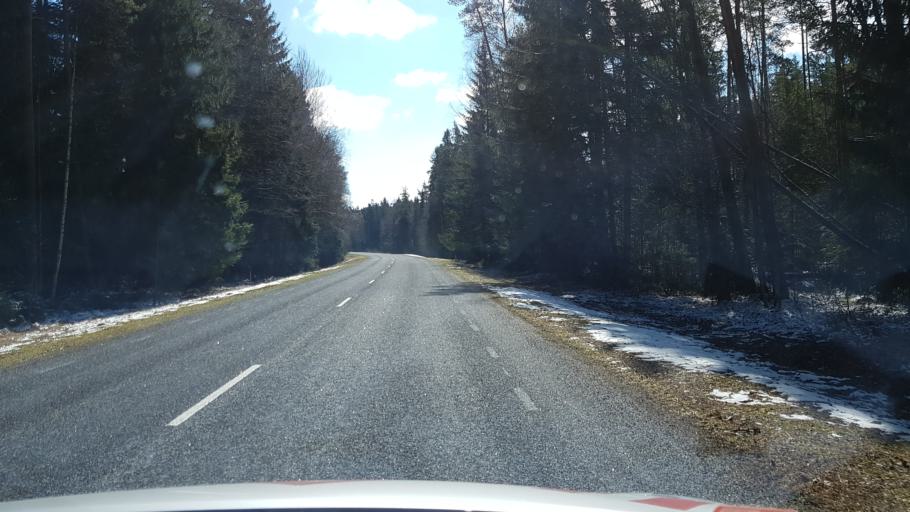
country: EE
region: Harju
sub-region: Loksa linn
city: Loksa
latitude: 59.5697
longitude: 25.9355
